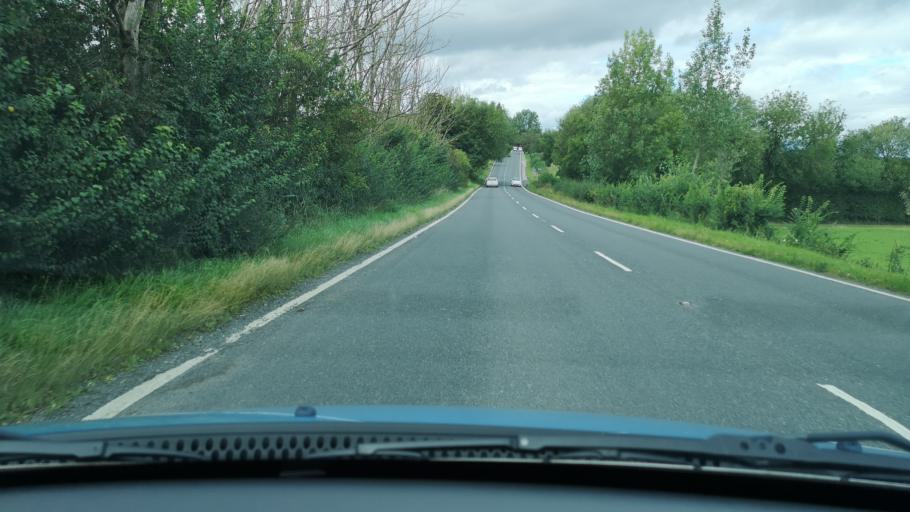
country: GB
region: England
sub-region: City and Borough of Wakefield
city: Low Ackworth
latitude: 53.6367
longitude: -1.3275
